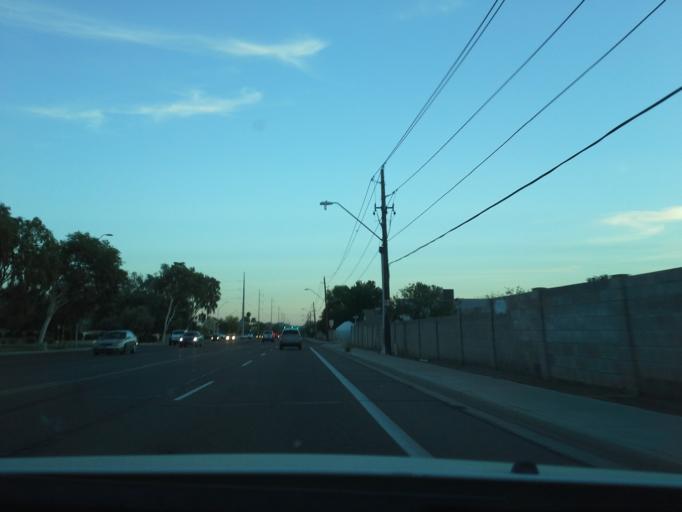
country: US
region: Arizona
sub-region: Maricopa County
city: Glendale
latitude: 33.6583
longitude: -112.0657
